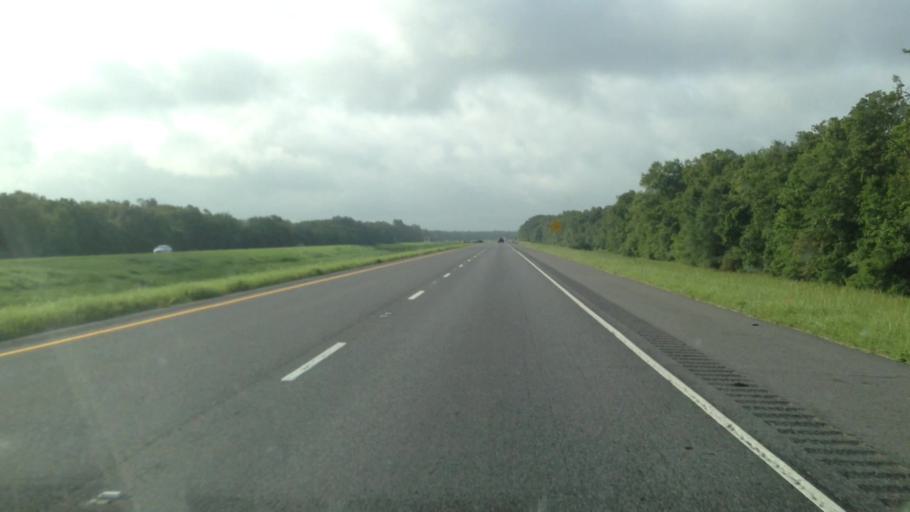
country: US
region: Louisiana
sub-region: Saint Landry Parish
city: Opelousas
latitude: 30.7069
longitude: -92.0957
